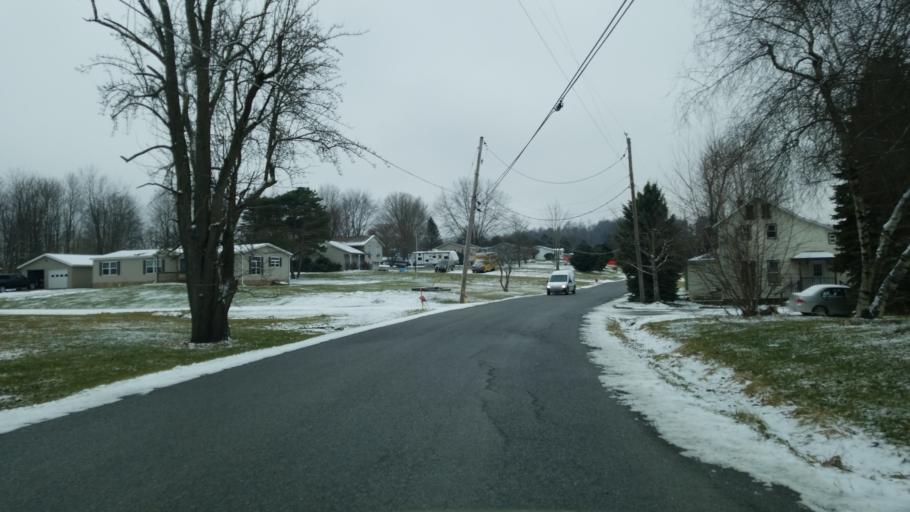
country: US
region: Pennsylvania
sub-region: Clearfield County
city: Sandy
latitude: 41.0783
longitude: -78.7904
